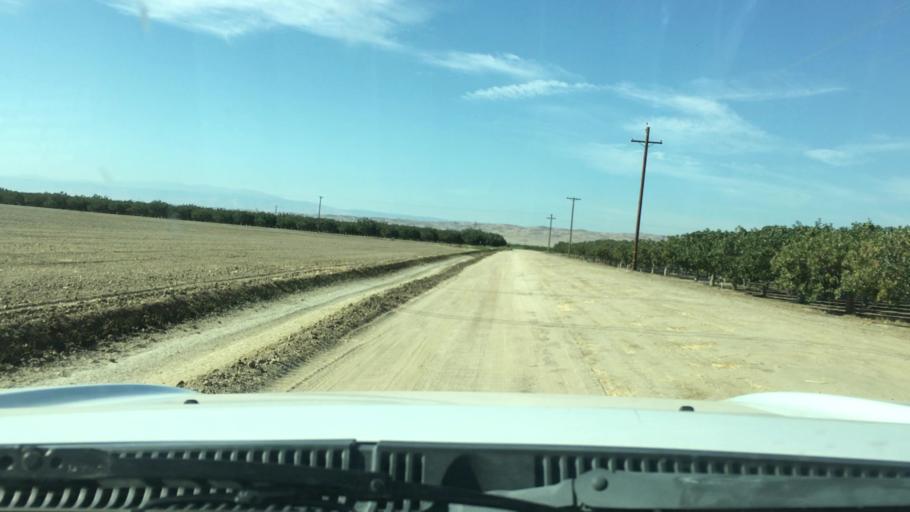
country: US
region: California
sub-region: Kern County
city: Buttonwillow
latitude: 35.3789
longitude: -119.4034
